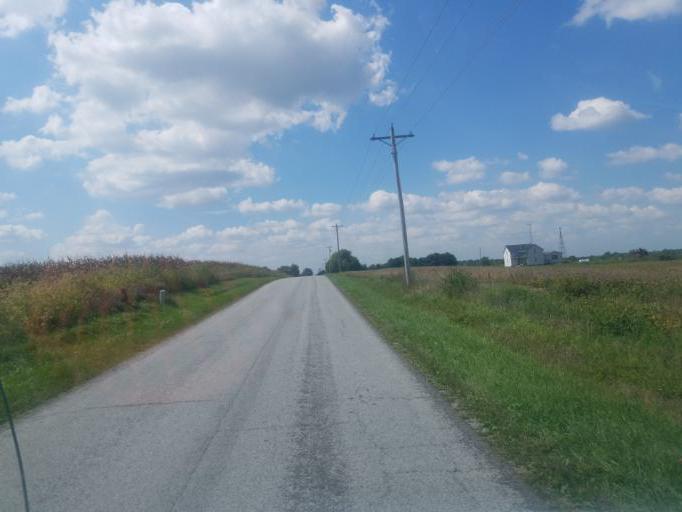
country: US
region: Ohio
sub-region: Hardin County
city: Ada
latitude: 40.6520
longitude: -83.9038
